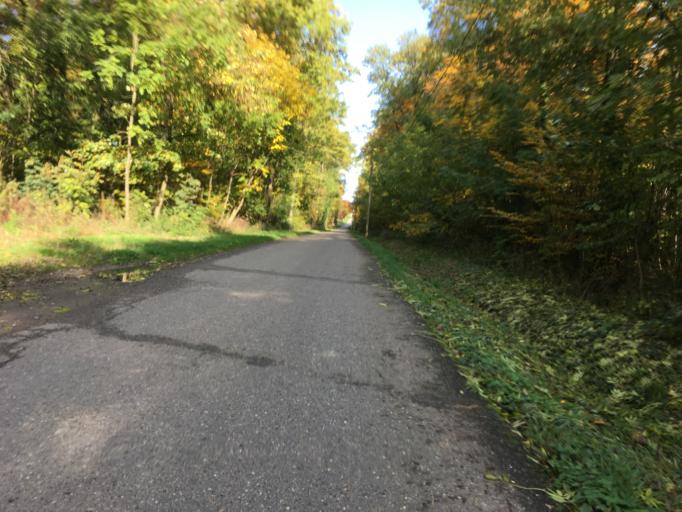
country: DE
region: Baden-Wuerttemberg
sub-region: Karlsruhe Region
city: Huffenhardt
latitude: 49.2663
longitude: 9.0440
